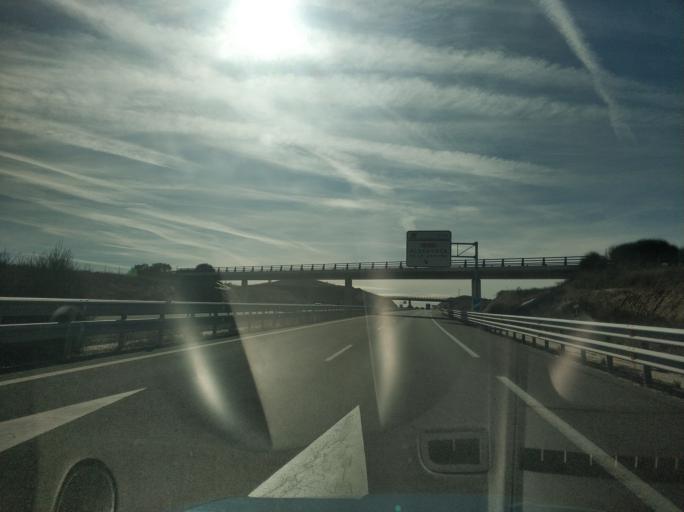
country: ES
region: Castille and Leon
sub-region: Provincia de Salamanca
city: Monterrubio de Armuna
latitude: 41.0336
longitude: -5.6711
